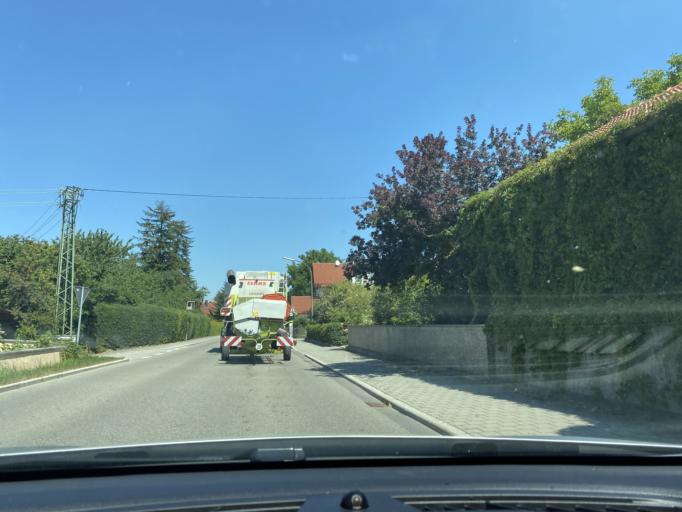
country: DE
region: Bavaria
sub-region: Upper Bavaria
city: Moosinning
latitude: 48.2707
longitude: 11.8457
